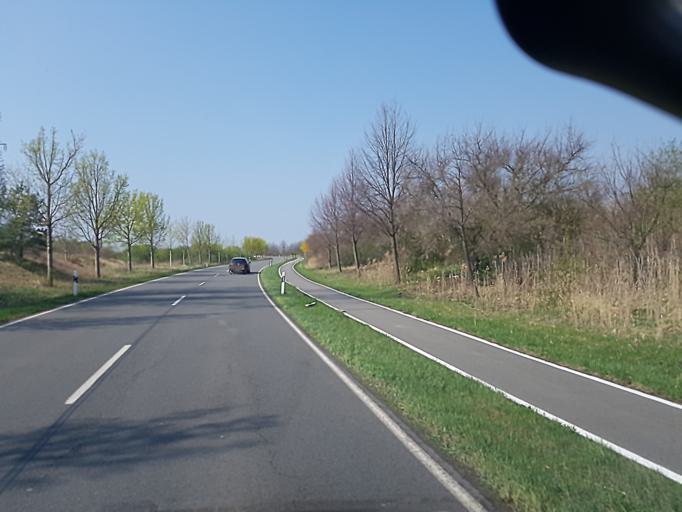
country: DE
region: Saxony-Anhalt
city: Grafenhainichen
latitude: 51.7355
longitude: 12.4483
